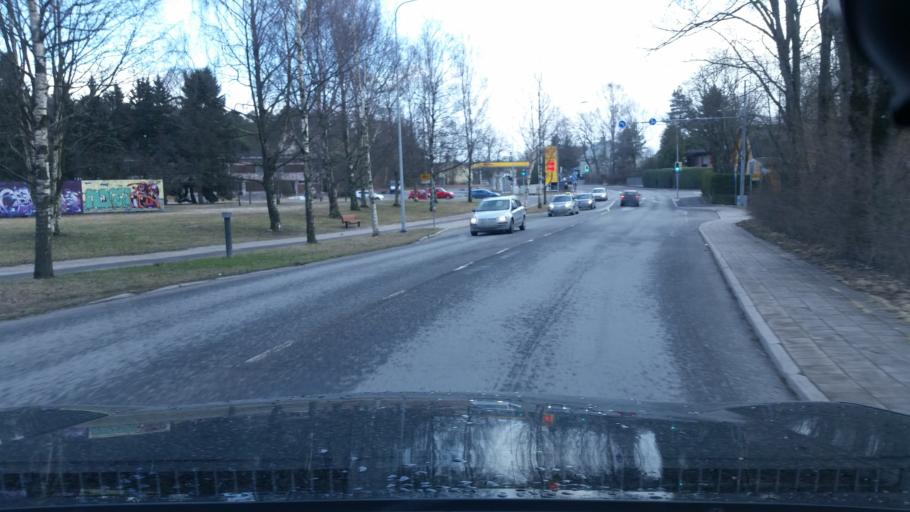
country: FI
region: Varsinais-Suomi
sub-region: Turku
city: Turku
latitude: 60.4368
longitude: 22.2623
